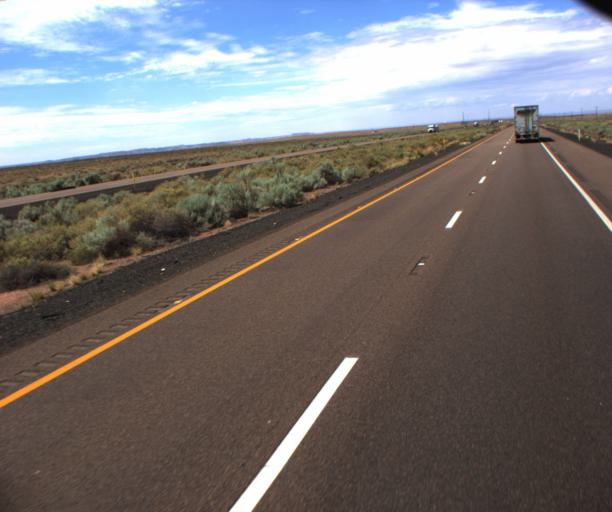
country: US
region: Arizona
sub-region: Navajo County
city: Holbrook
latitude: 35.0462
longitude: -109.8064
